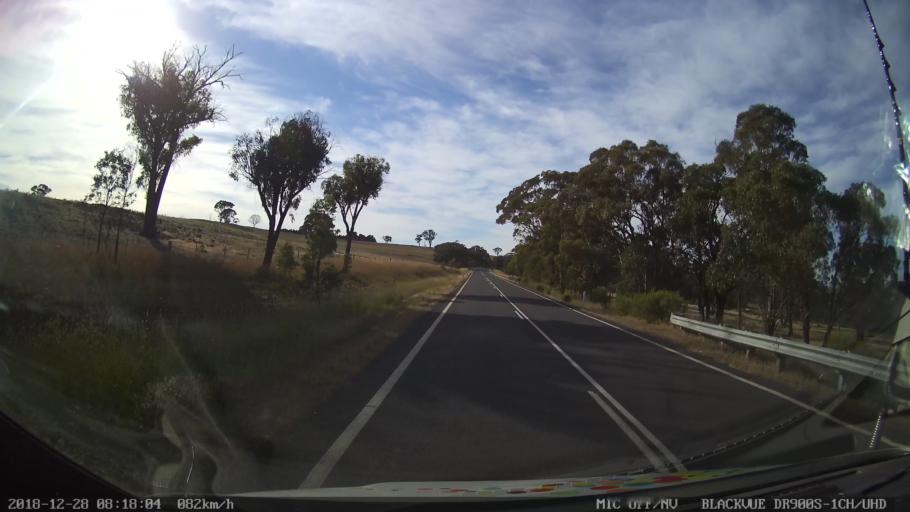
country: AU
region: New South Wales
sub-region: Blayney
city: Blayney
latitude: -33.8430
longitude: 149.3466
